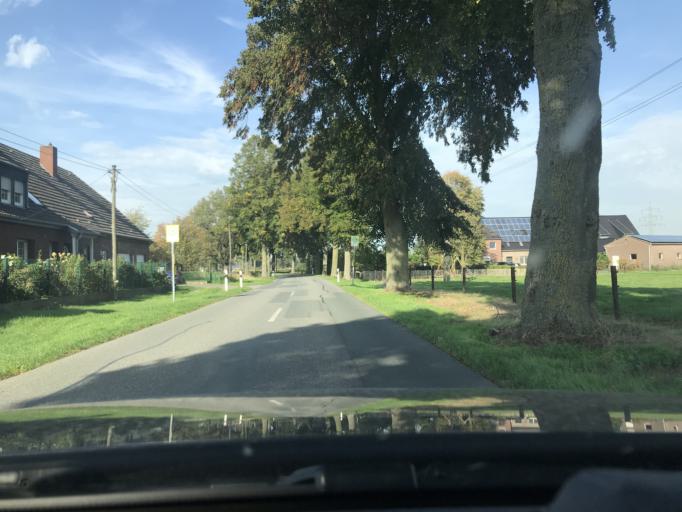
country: DE
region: North Rhine-Westphalia
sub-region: Regierungsbezirk Dusseldorf
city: Uedem
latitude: 51.6981
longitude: 6.2669
